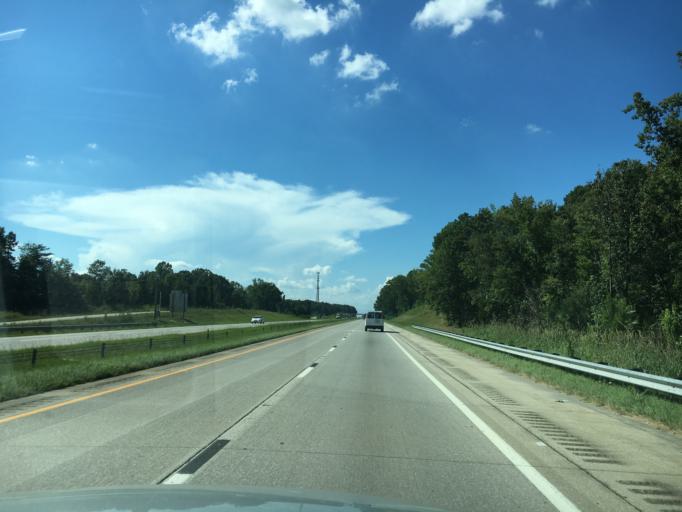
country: US
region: South Carolina
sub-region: Laurens County
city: Watts Mills
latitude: 34.5604
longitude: -82.0211
